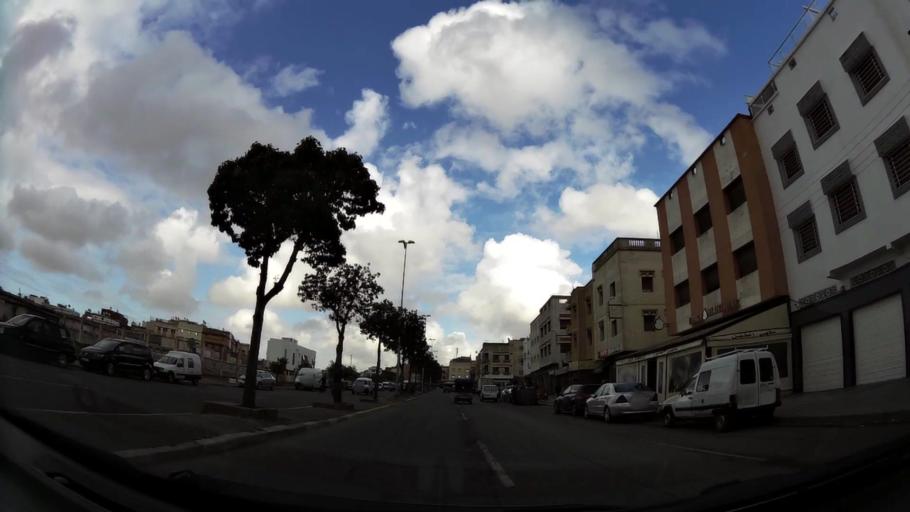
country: MA
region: Grand Casablanca
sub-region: Casablanca
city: Casablanca
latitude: 33.5474
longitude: -7.5919
